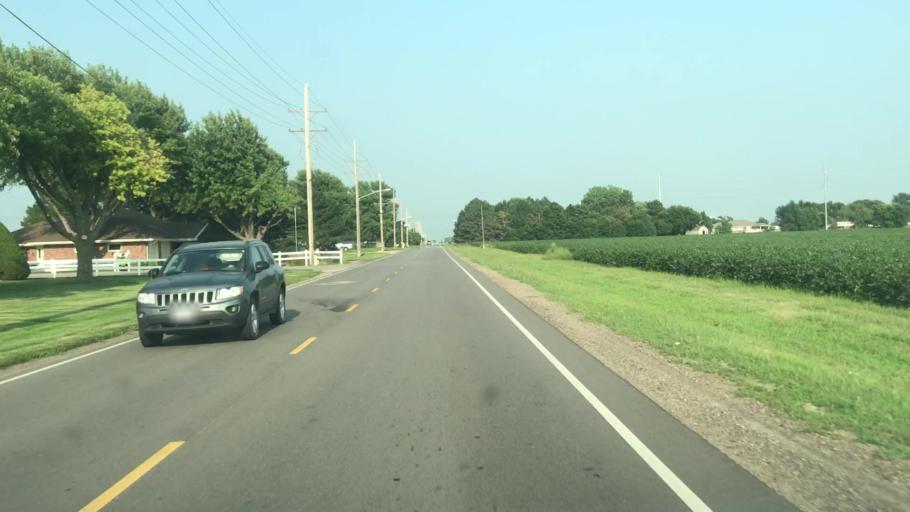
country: US
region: Nebraska
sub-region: Hall County
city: Grand Island
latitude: 40.9455
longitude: -98.3290
